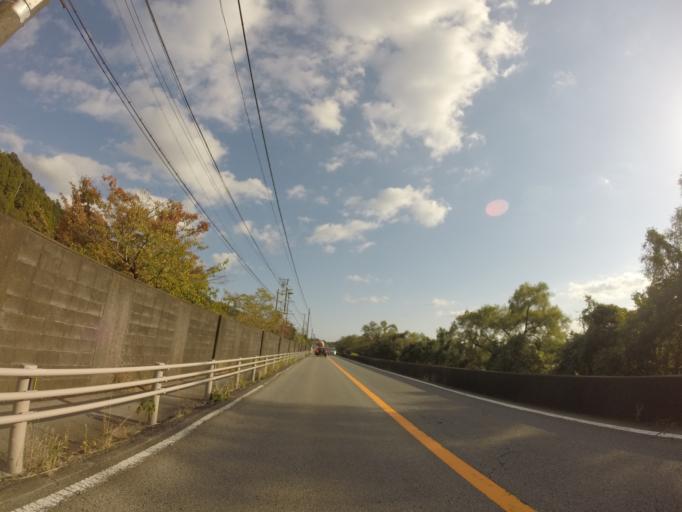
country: JP
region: Shizuoka
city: Kanaya
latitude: 34.8545
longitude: 138.1373
